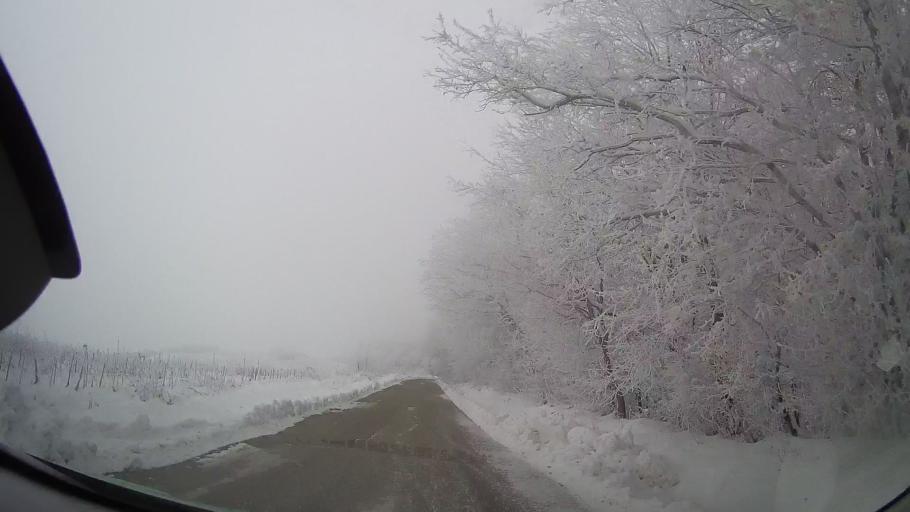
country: RO
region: Iasi
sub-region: Comuna Dagata
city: Dagata
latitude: 46.9149
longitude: 27.1820
